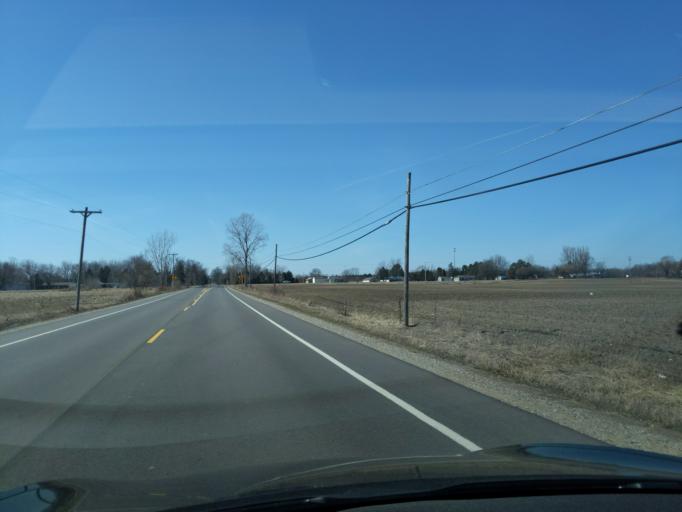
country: US
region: Michigan
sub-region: Eaton County
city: Grand Ledge
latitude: 42.7264
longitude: -84.7352
